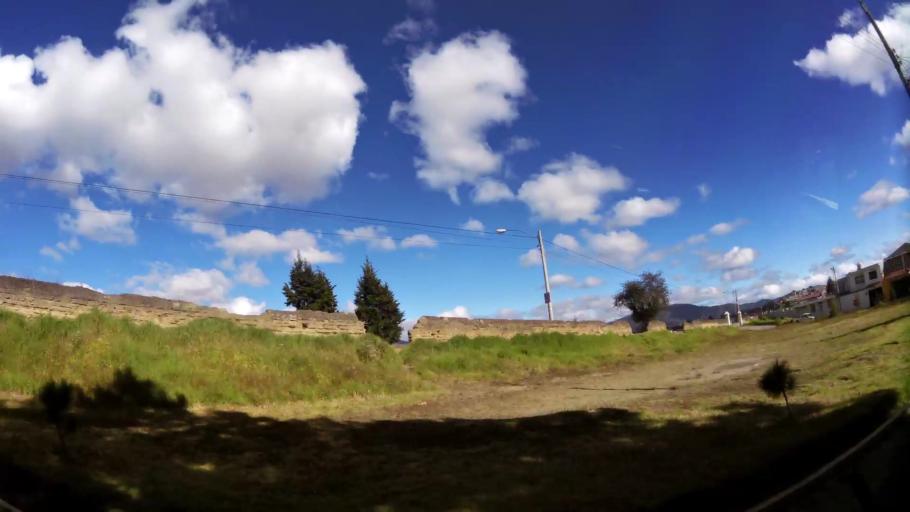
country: GT
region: Quetzaltenango
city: Quetzaltenango
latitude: 14.8298
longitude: -91.5109
